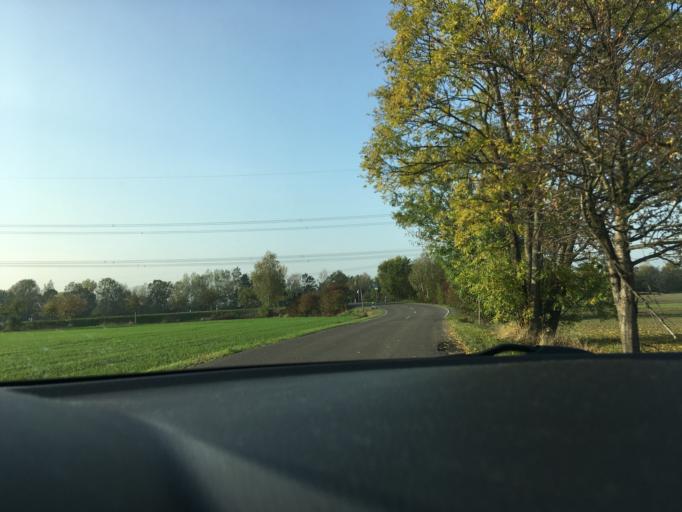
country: DE
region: Saxony
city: Rotha
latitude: 51.1859
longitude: 12.4293
